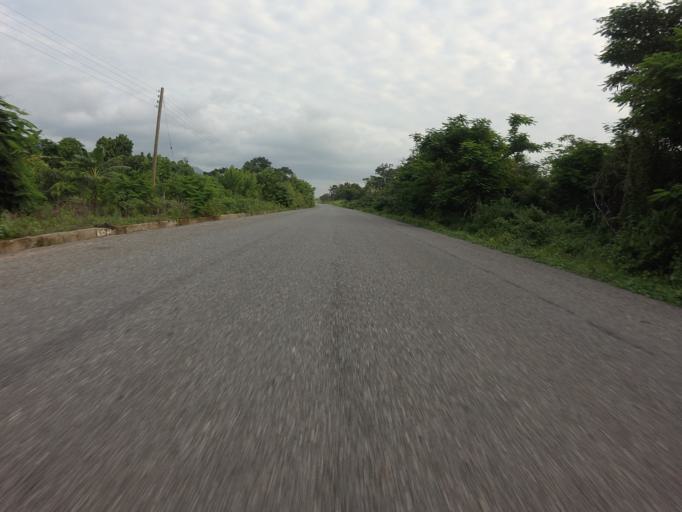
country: GH
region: Volta
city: Kpandu
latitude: 6.8620
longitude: 0.3973
